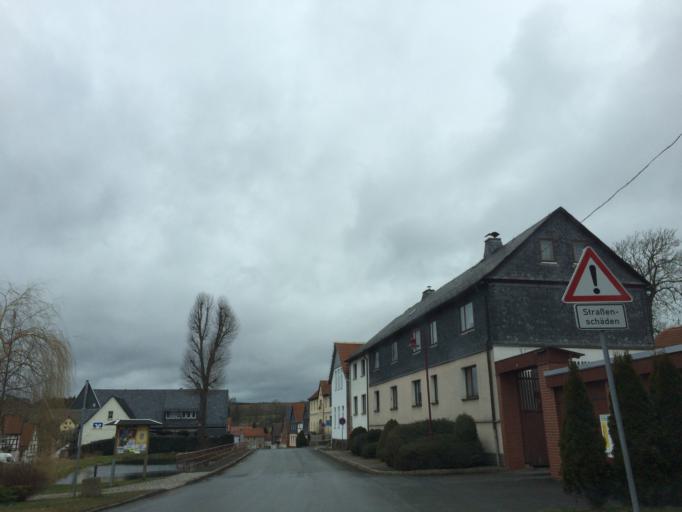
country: DE
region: Thuringia
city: Knau
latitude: 50.6528
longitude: 11.7188
